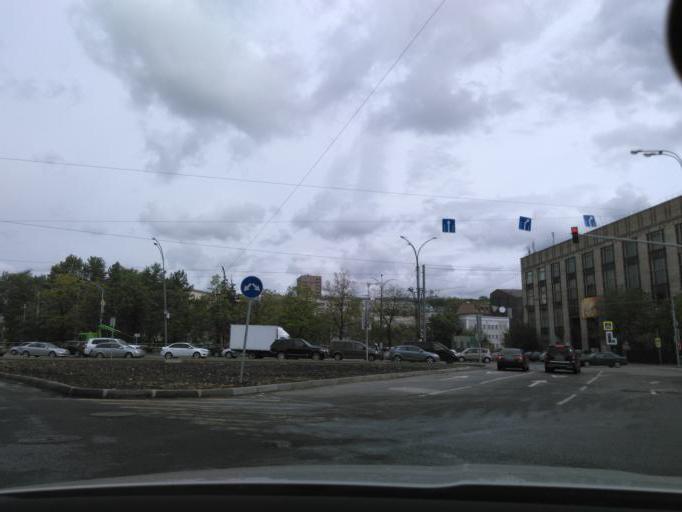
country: RU
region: Moscow
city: Zamoskvorech'ye
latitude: 55.7478
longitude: 37.6465
